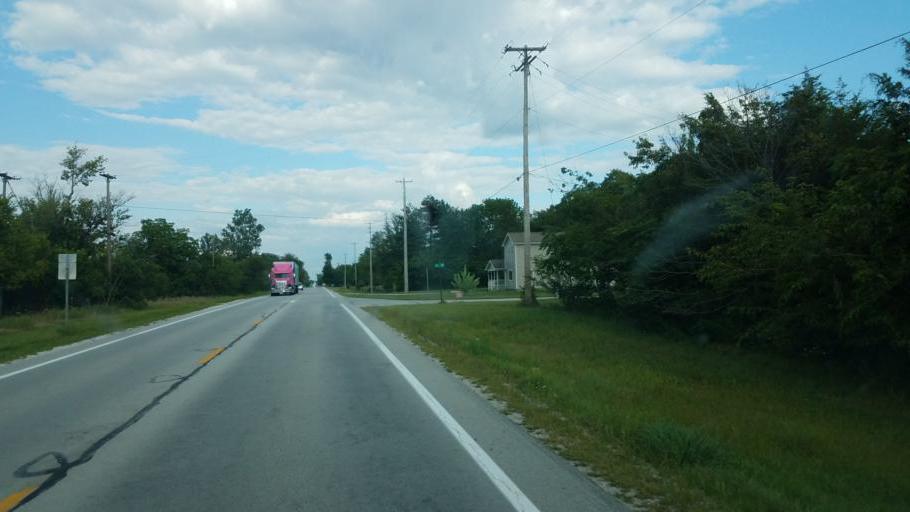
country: US
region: Ohio
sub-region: Sandusky County
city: Gibsonburg
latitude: 41.3410
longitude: -83.3312
